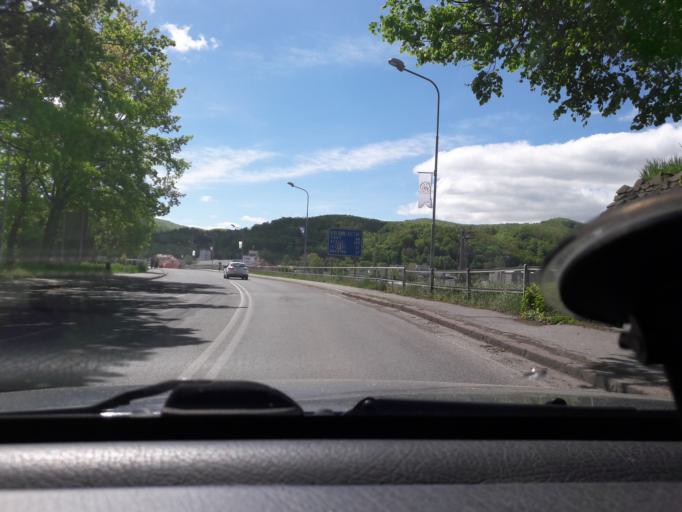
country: SK
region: Banskobystricky
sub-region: Okres Banska Bystrica
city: Zvolen
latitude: 48.5729
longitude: 19.1263
